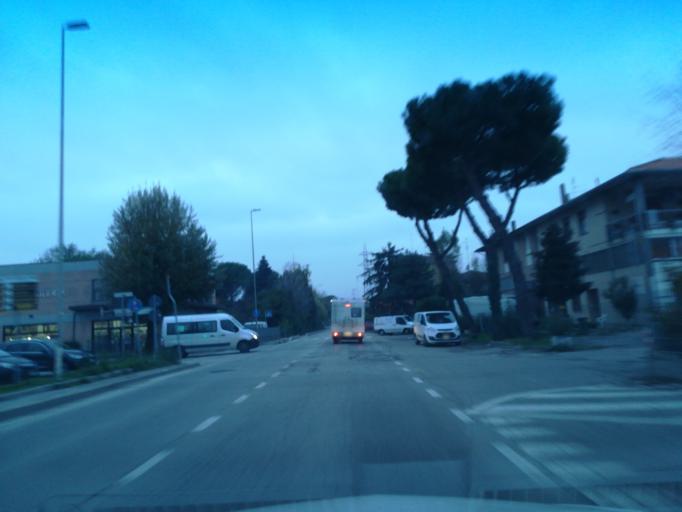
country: IT
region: Emilia-Romagna
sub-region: Provincia di Ravenna
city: Faenza
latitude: 44.2988
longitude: 11.8677
